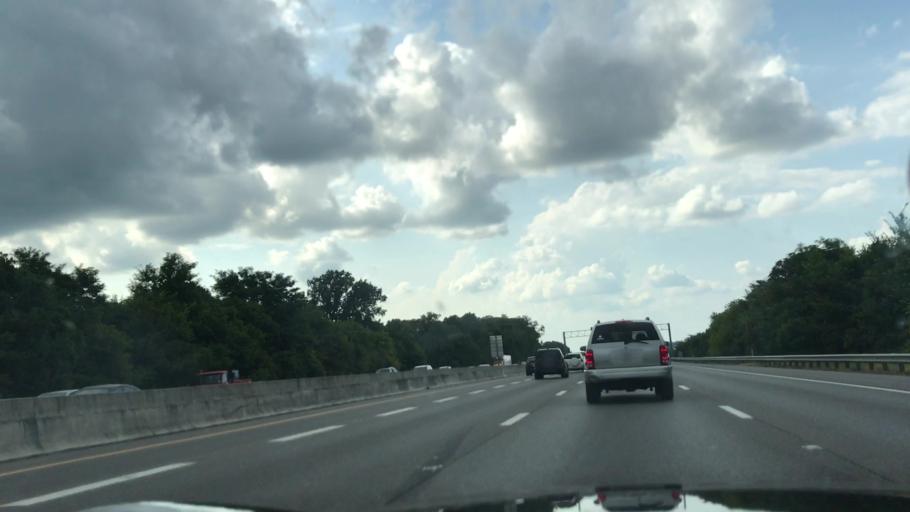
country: US
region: Tennessee
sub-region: Rutherford County
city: La Vergne
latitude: 36.0325
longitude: -86.6405
